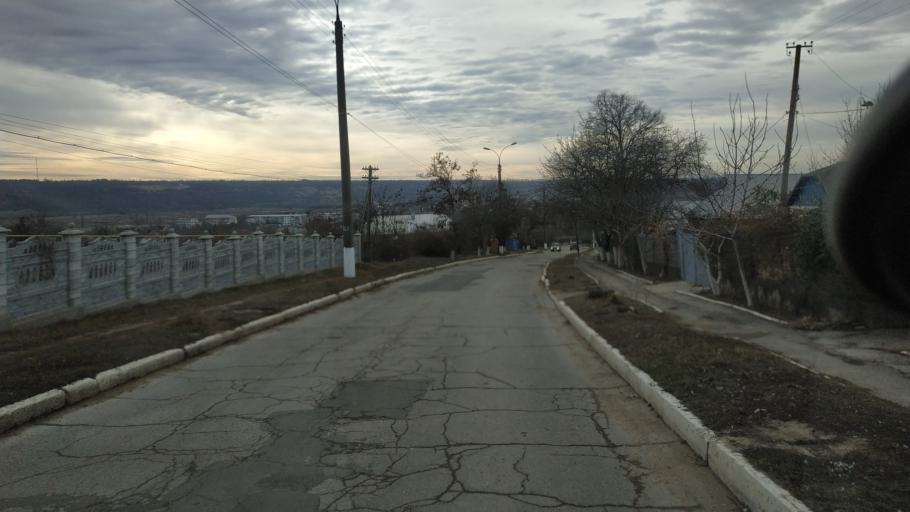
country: MD
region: Criuleni
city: Criuleni
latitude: 47.2181
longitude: 29.1583
